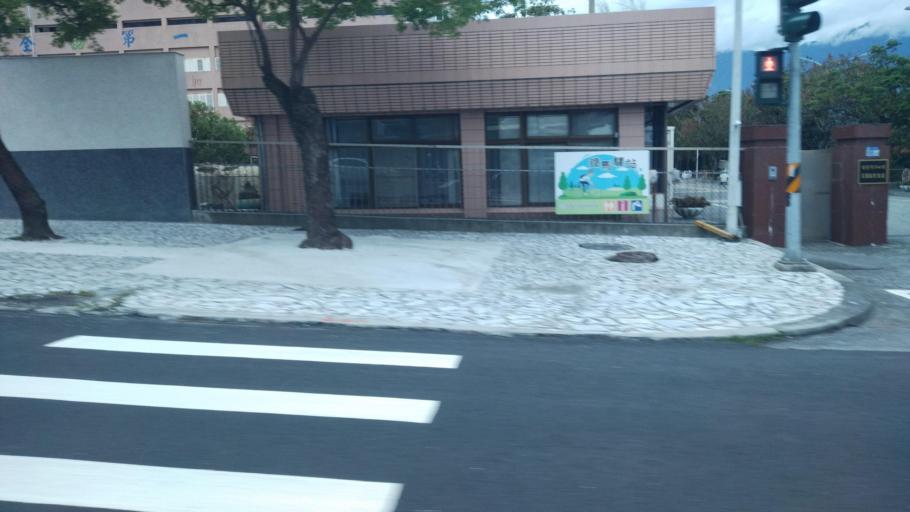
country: TW
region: Taiwan
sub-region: Hualien
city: Hualian
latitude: 24.0062
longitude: 121.6184
